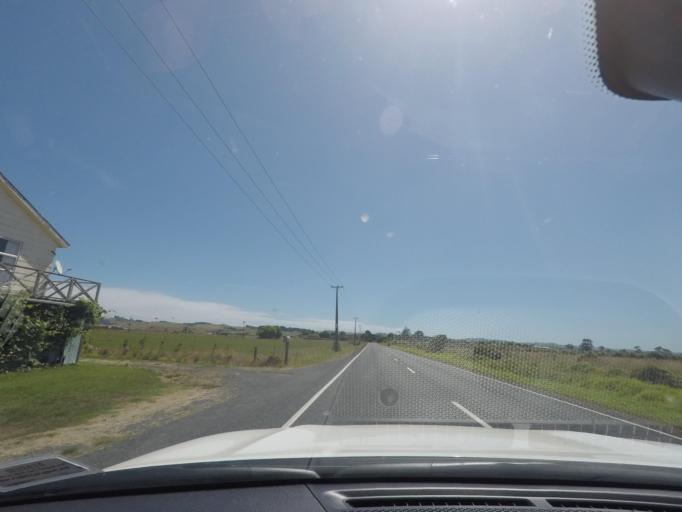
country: NZ
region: Auckland
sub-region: Auckland
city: Parakai
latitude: -36.6508
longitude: 174.4181
